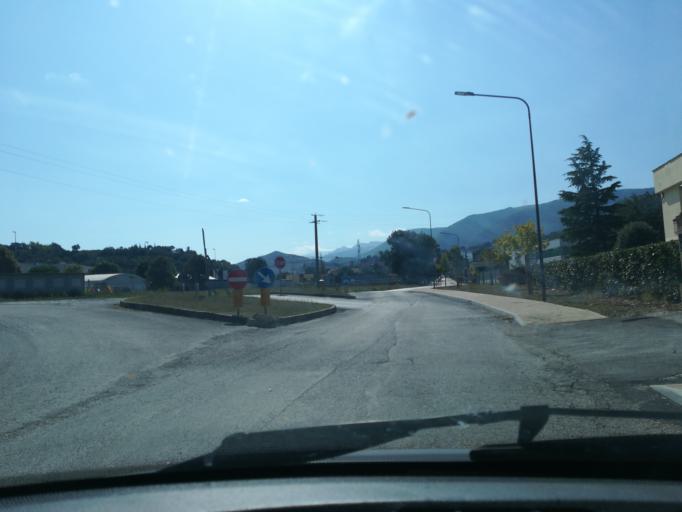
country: IT
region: The Marches
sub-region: Provincia di Macerata
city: Caldarola
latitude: 43.1485
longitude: 13.2241
